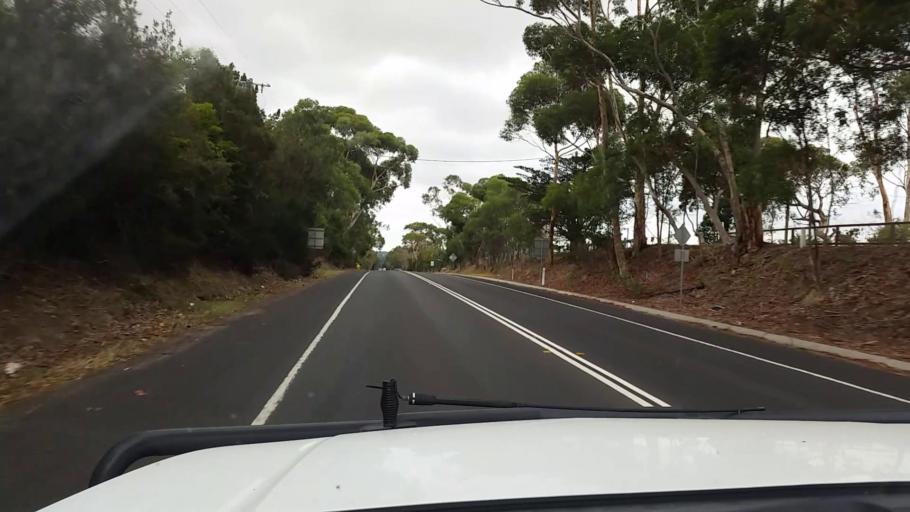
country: AU
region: Victoria
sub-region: Mornington Peninsula
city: Somerville
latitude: -38.2185
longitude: 145.1719
